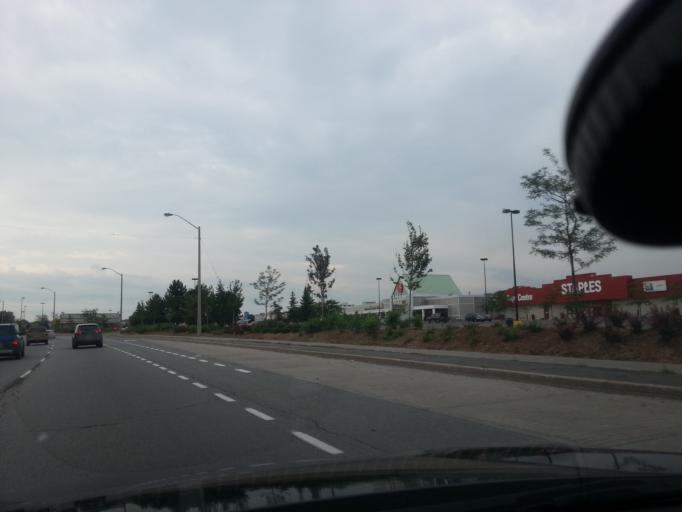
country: CA
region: Ontario
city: Ottawa
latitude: 45.3595
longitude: -75.6564
